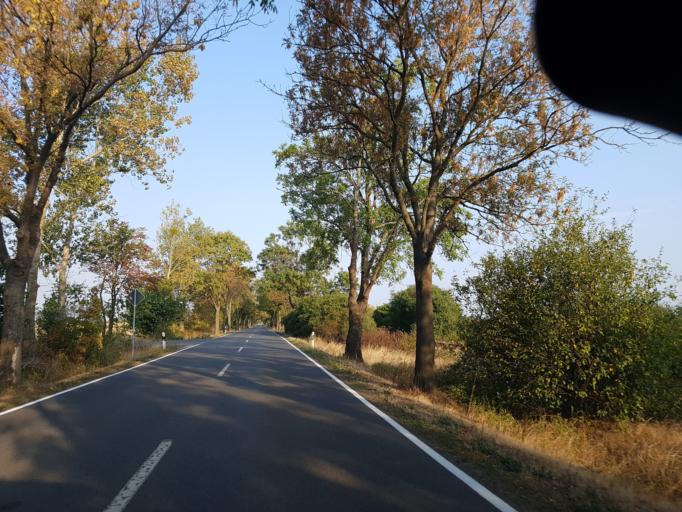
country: DE
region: Saxony-Anhalt
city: Kemberg
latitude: 51.7985
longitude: 12.6931
